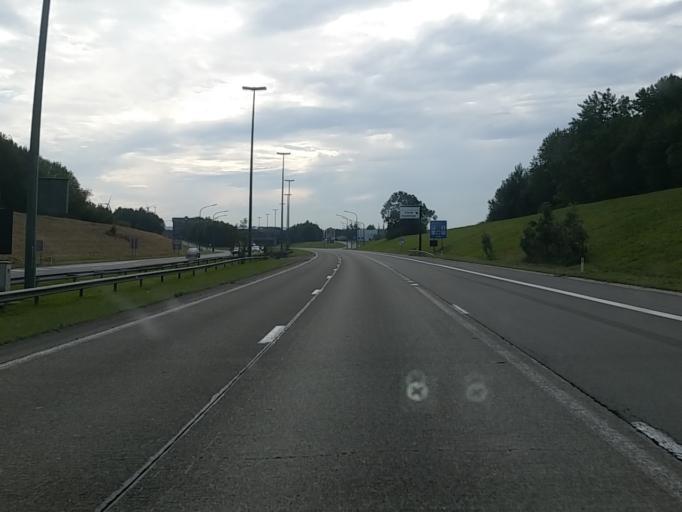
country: BE
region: Wallonia
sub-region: Province du Luxembourg
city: Arlon
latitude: 49.6469
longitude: 5.8230
